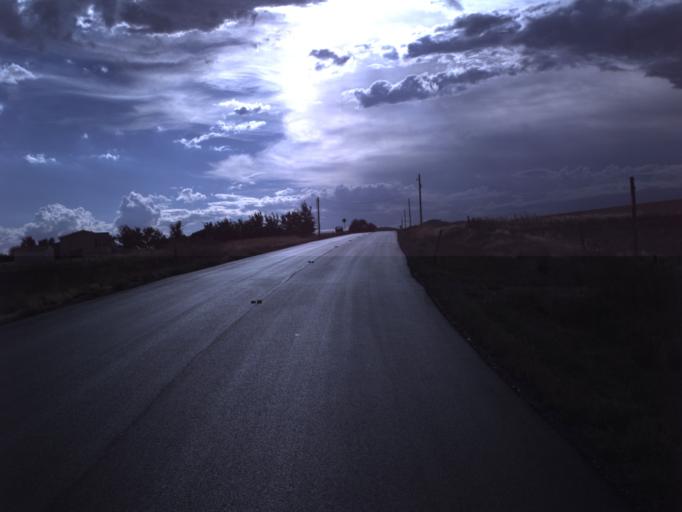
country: US
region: Utah
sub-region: Cache County
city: Benson
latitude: 41.8629
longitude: -111.9604
